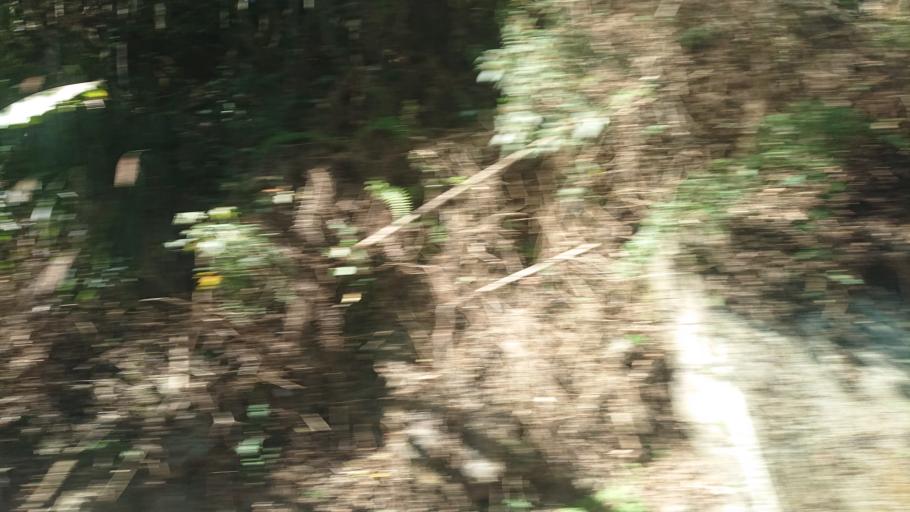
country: TW
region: Taiwan
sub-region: Chiayi
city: Jiayi Shi
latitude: 23.5348
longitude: 120.6375
